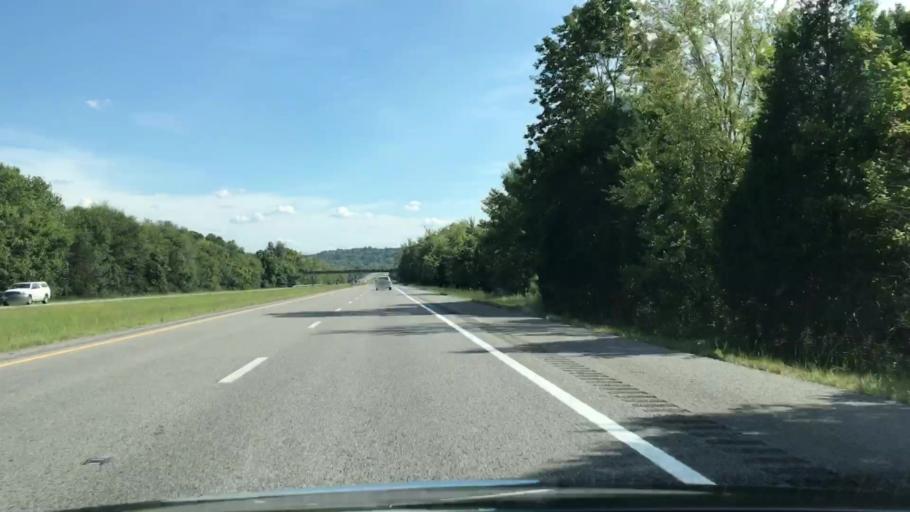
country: US
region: Alabama
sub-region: Limestone County
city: Ardmore
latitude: 35.1420
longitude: -86.8786
